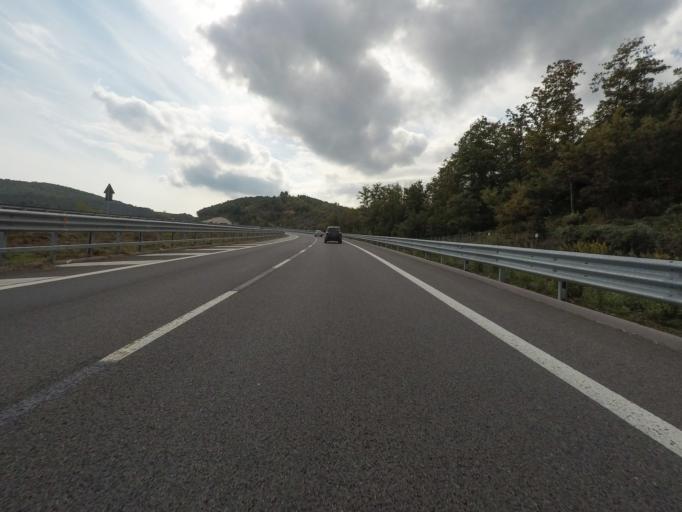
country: IT
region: Tuscany
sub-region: Provincia di Siena
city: Murlo
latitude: 43.1096
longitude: 11.2953
